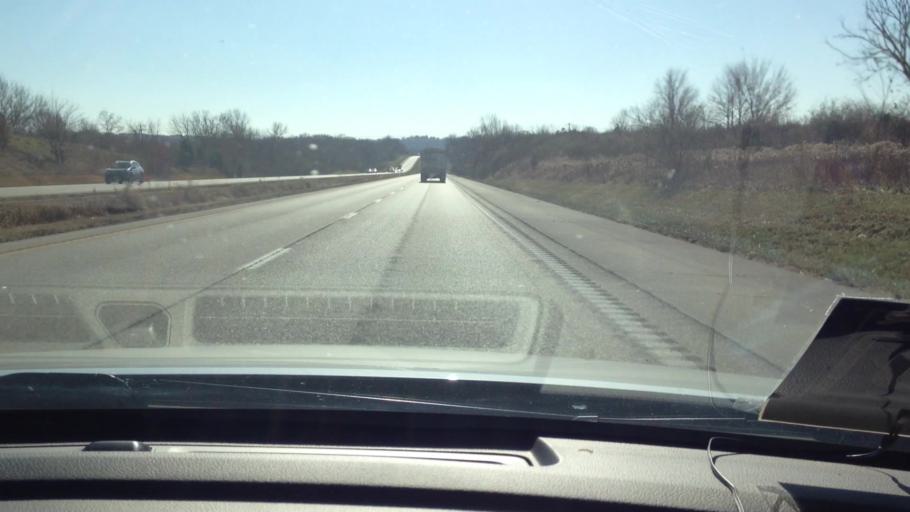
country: US
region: Missouri
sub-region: Platte County
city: Platte City
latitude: 39.3995
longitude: -94.7898
